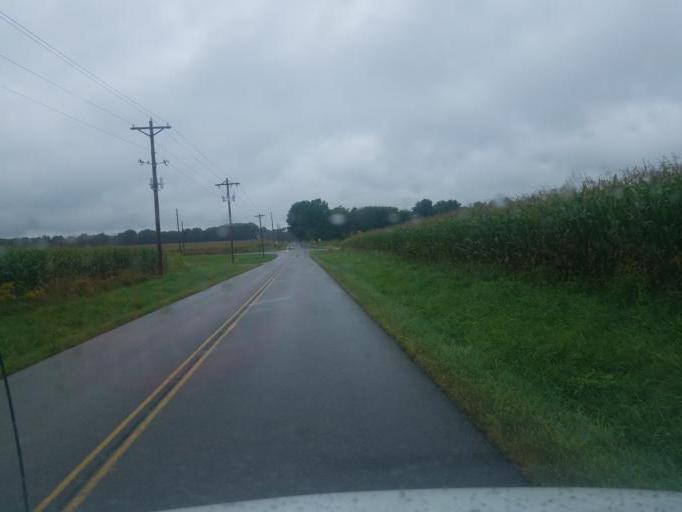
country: US
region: Ohio
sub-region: Medina County
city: Lodi
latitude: 40.9746
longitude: -81.9945
